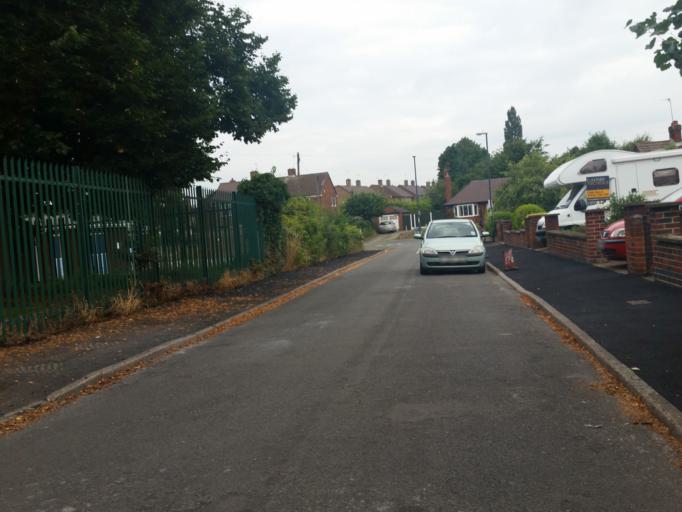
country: GB
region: England
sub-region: Derbyshire
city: Borrowash
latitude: 52.8939
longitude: -1.4193
